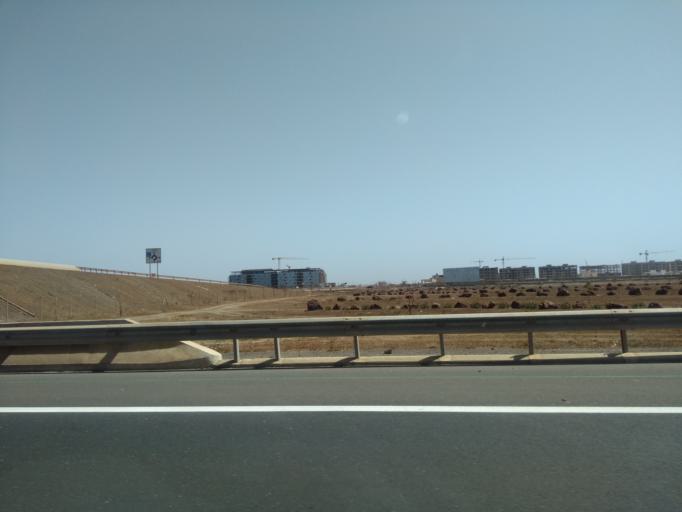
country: SN
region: Thies
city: Thies
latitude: 14.7329
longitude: -17.2073
